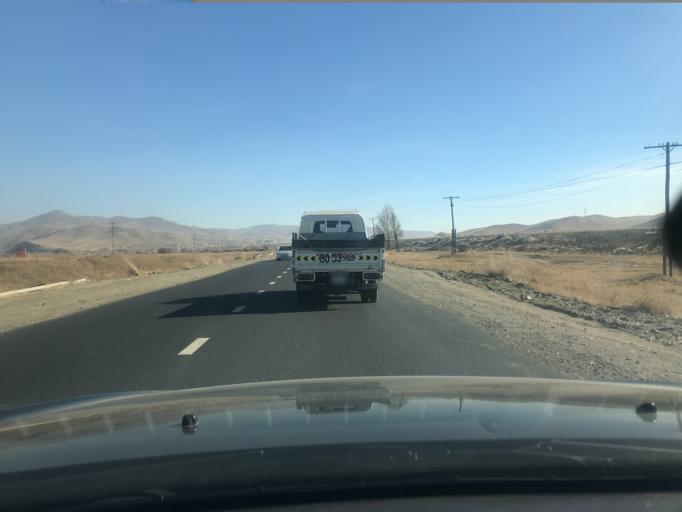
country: MN
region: Ulaanbaatar
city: Ulaanbaatar
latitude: 47.8973
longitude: 107.0458
